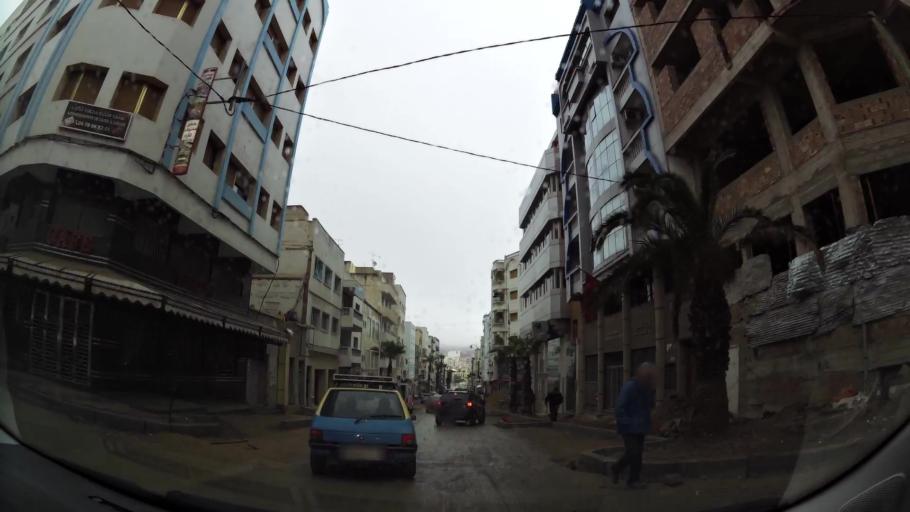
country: MA
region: Taza-Al Hoceima-Taounate
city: Al Hoceima
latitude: 35.2422
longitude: -3.9300
